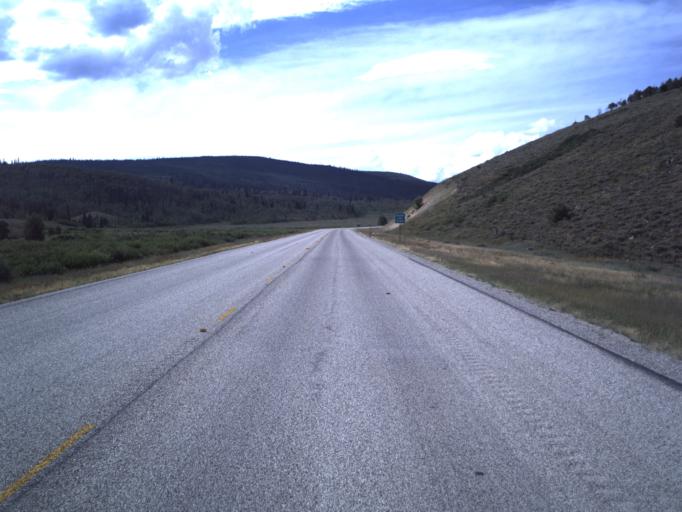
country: US
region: Utah
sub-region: Wasatch County
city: Heber
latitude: 40.2865
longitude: -111.2424
